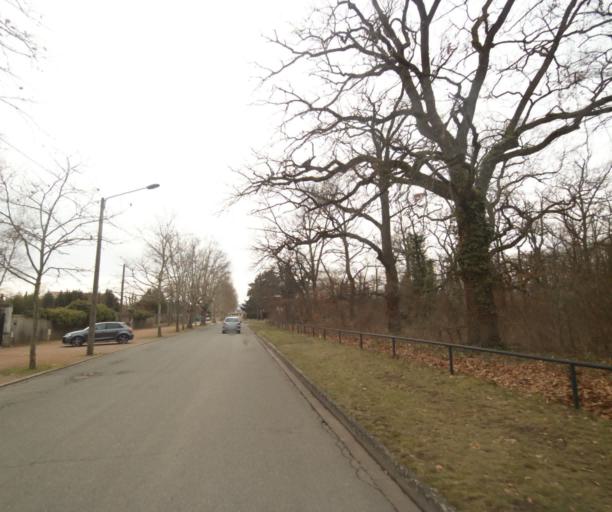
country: FR
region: Rhone-Alpes
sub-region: Departement de la Loire
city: Mably
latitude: 46.0633
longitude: 4.0771
